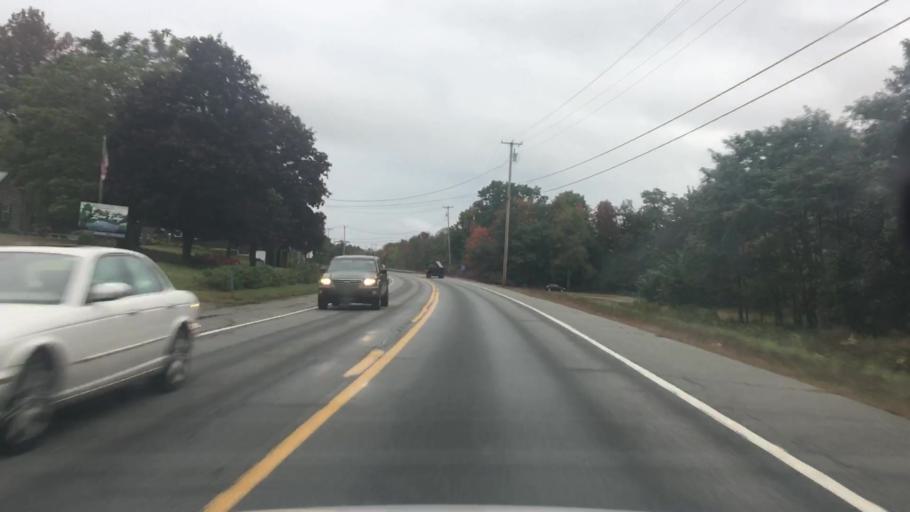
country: US
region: Maine
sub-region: Kennebec County
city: Belgrade
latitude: 44.4413
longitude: -69.8315
